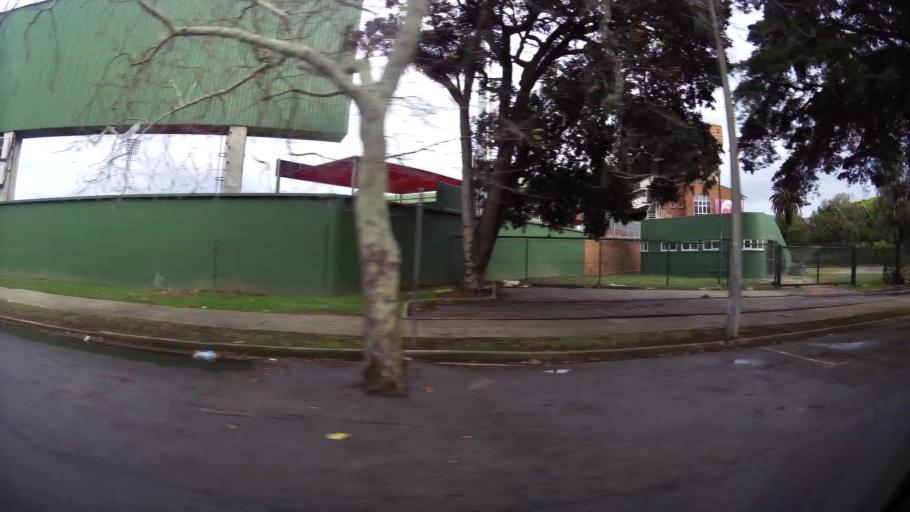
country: ZA
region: Eastern Cape
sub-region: Nelson Mandela Bay Metropolitan Municipality
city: Port Elizabeth
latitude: -33.9662
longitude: 25.6111
